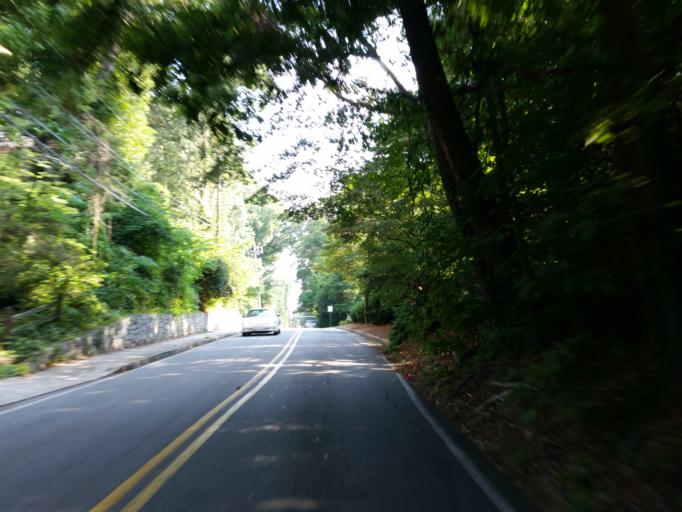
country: US
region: Georgia
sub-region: DeKalb County
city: North Atlanta
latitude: 33.8768
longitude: -84.3578
